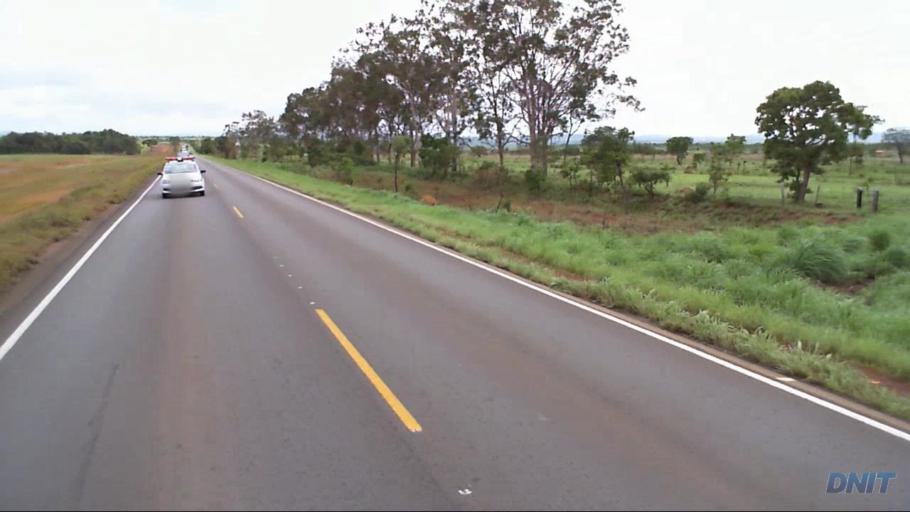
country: BR
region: Goias
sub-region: Padre Bernardo
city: Padre Bernardo
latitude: -15.3188
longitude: -48.2293
